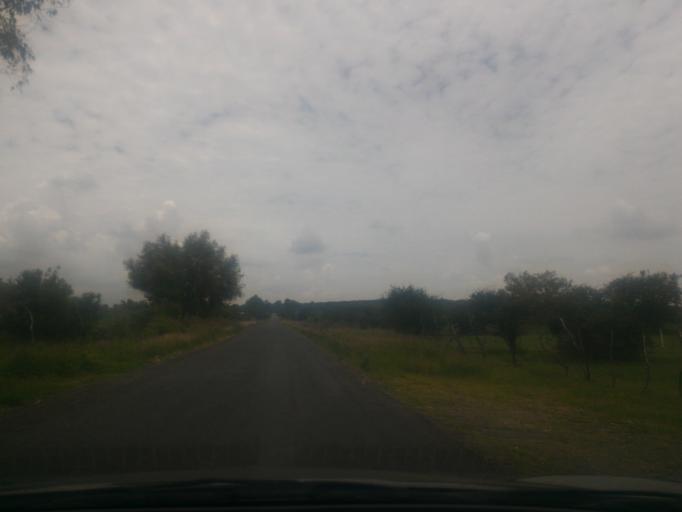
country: MX
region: Guanajuato
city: Ciudad Manuel Doblado
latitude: 20.8275
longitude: -102.0494
